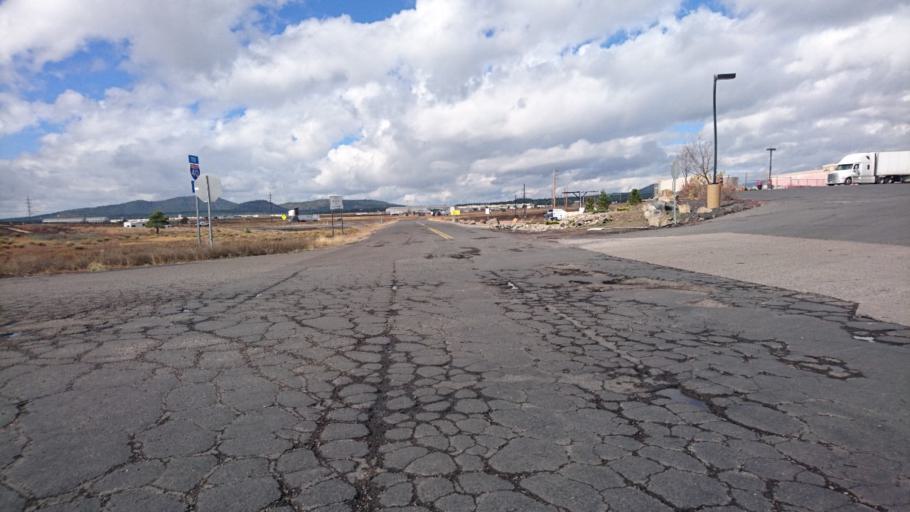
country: US
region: Arizona
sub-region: Coconino County
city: Parks
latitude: 35.2379
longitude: -111.8223
